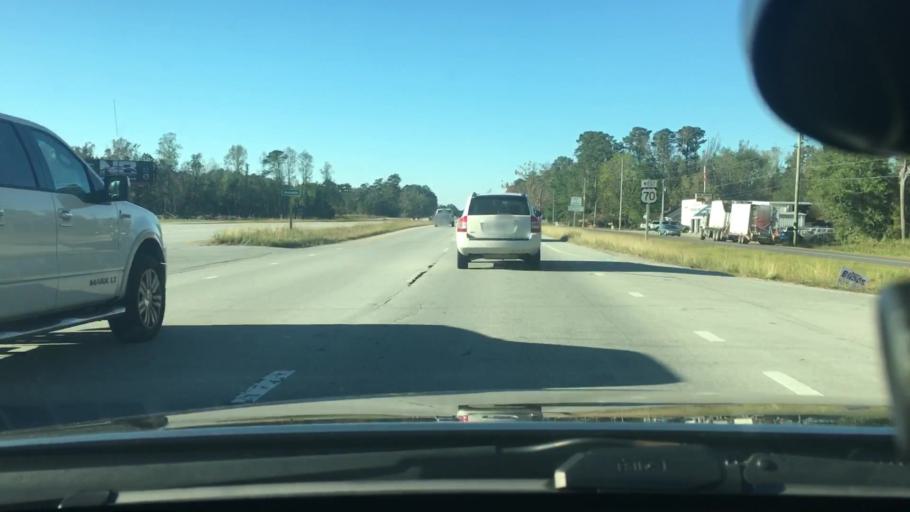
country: US
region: North Carolina
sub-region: Craven County
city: Neuse Forest
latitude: 34.9968
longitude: -76.9847
